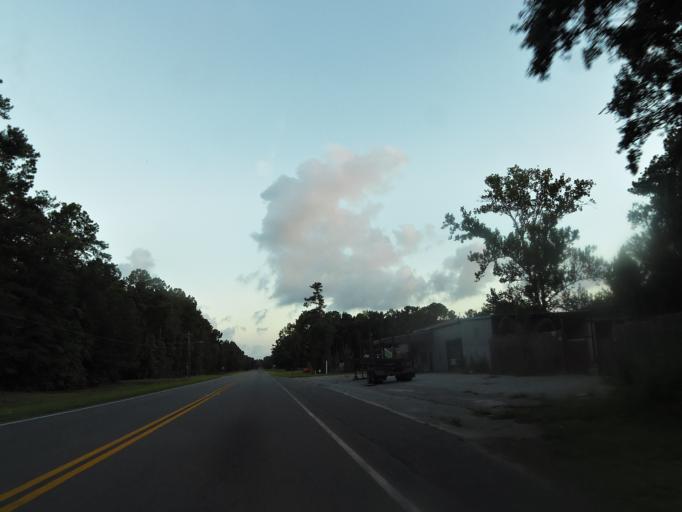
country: US
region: Georgia
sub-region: Camden County
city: Kingsland
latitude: 30.7911
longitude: -81.6885
